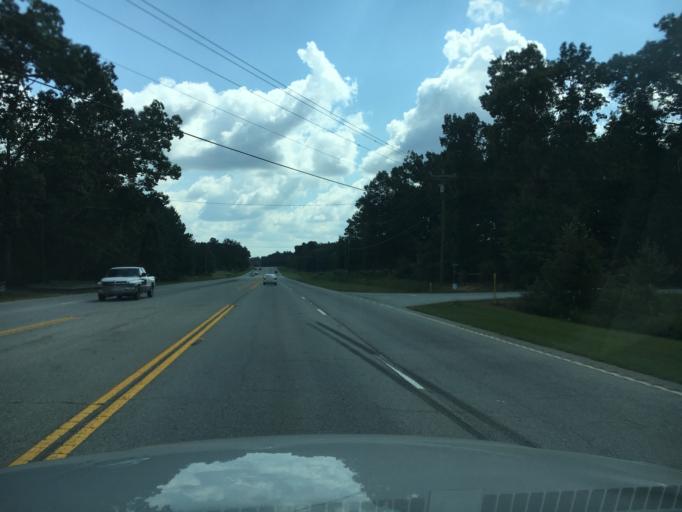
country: US
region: South Carolina
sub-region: Anderson County
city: Williamston
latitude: 34.6165
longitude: -82.3795
